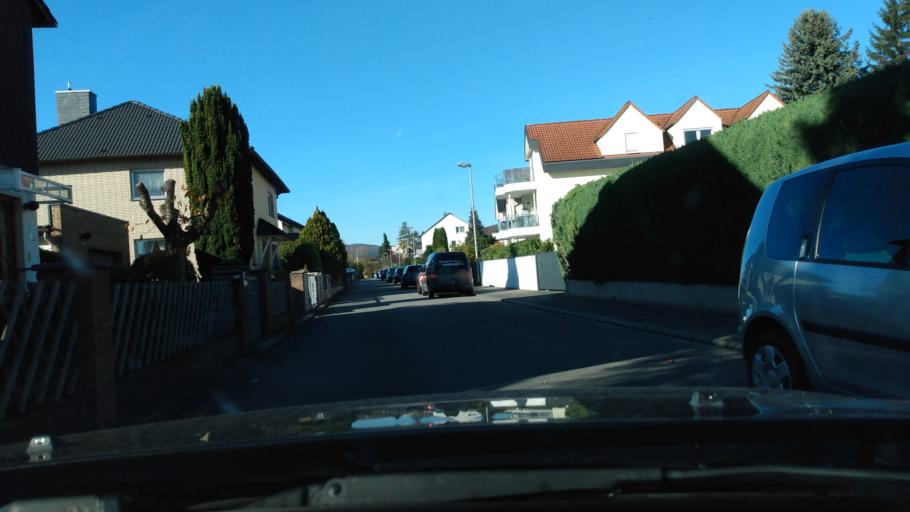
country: DE
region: Hesse
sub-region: Regierungsbezirk Darmstadt
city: Kriftel
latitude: 50.0837
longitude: 8.4635
